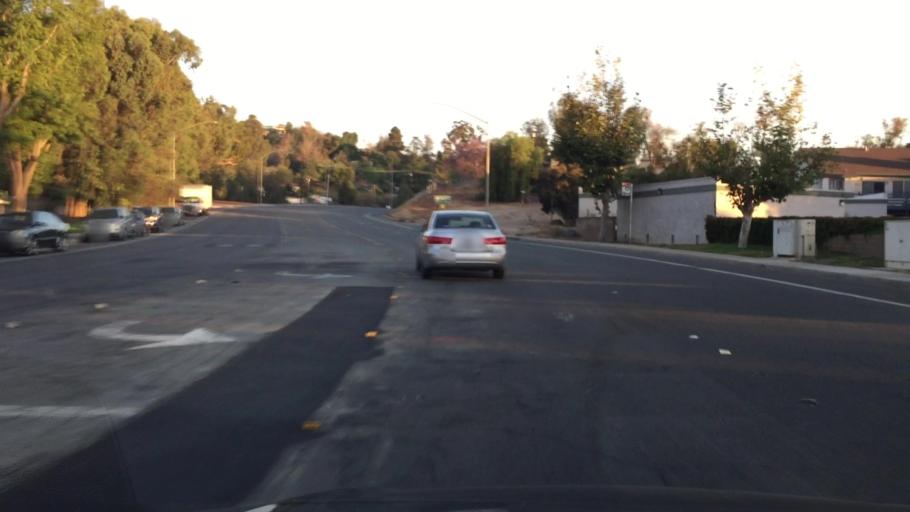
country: US
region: California
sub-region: San Diego County
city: Bostonia
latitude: 32.7822
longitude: -116.9280
